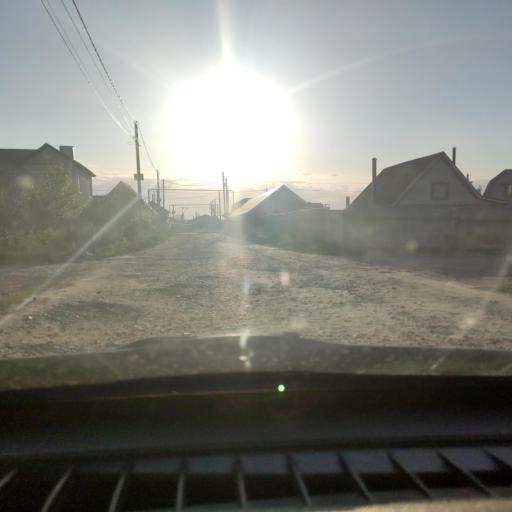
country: RU
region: Samara
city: Tol'yatti
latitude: 53.5635
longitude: 49.4044
